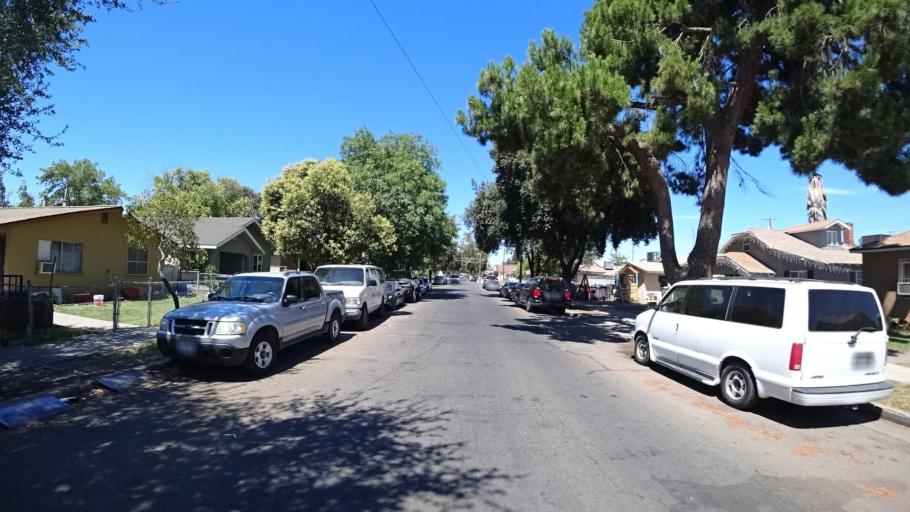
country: US
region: California
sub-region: Fresno County
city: Fresno
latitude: 36.7495
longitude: -119.7665
